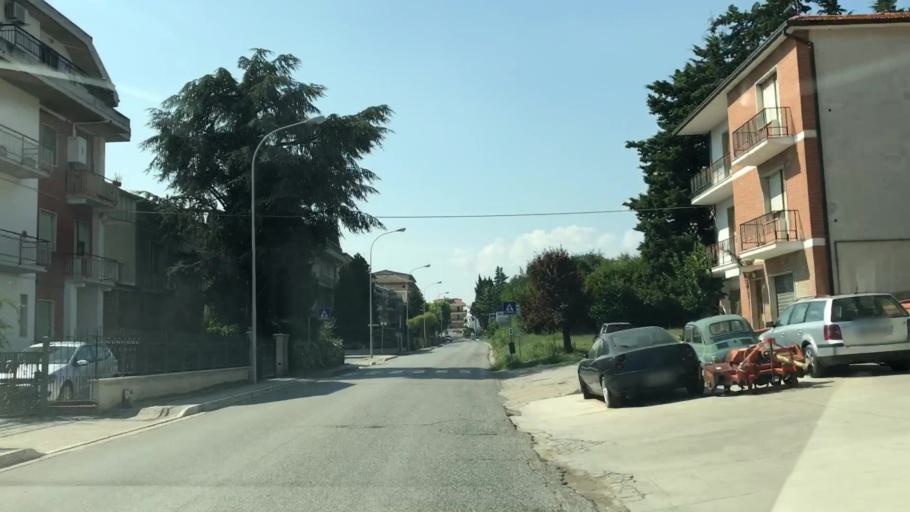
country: IT
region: The Marches
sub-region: Provincia di Ascoli Piceno
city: Stella
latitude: 42.8886
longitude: 13.8188
